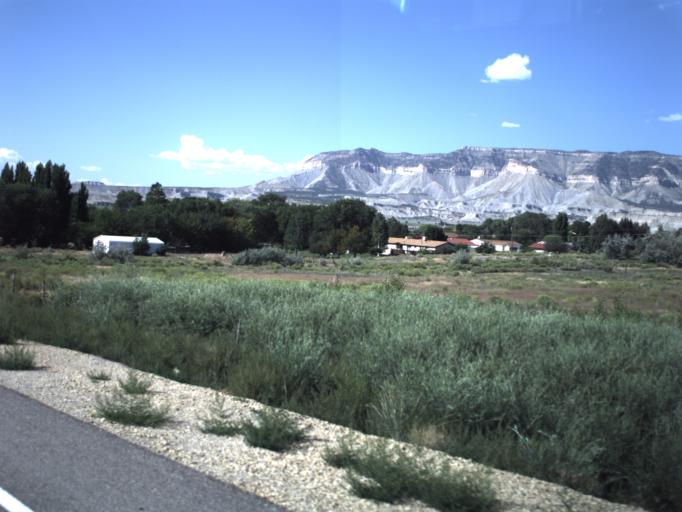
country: US
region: Utah
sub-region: Emery County
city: Ferron
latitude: 39.0975
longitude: -111.1322
